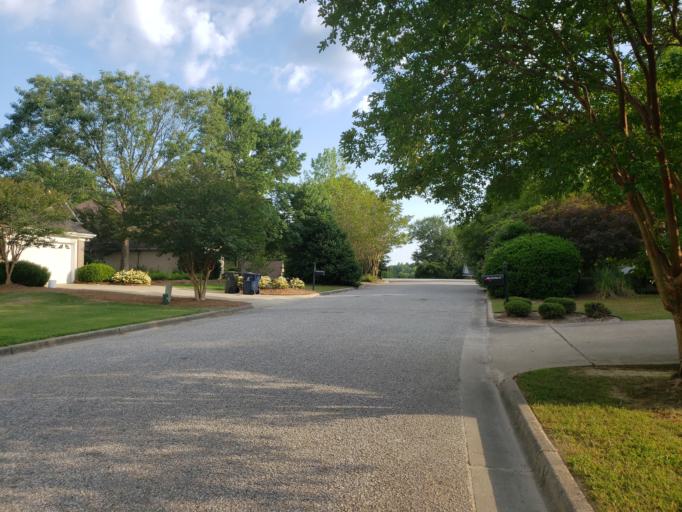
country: US
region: Alabama
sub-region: Lee County
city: Auburn
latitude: 32.5854
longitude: -85.4574
